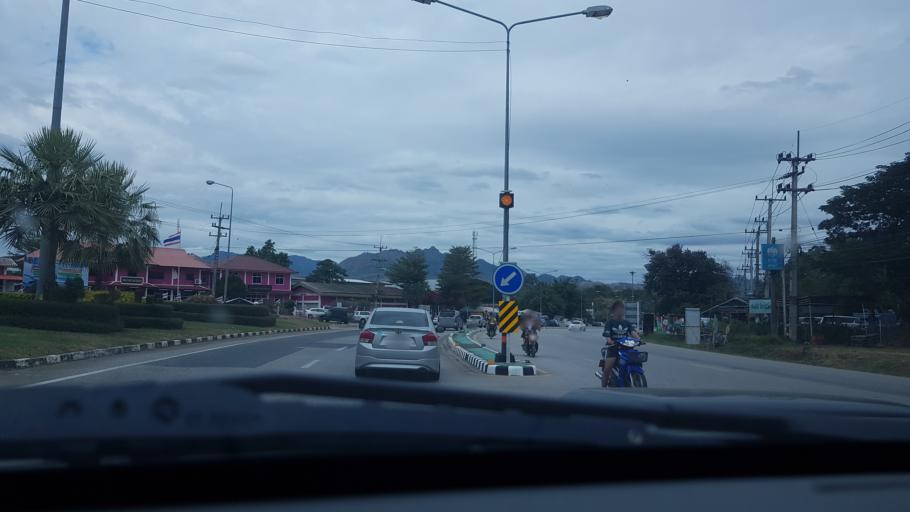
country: TH
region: Phetchabun
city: Phetchabun
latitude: 16.2619
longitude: 101.0480
